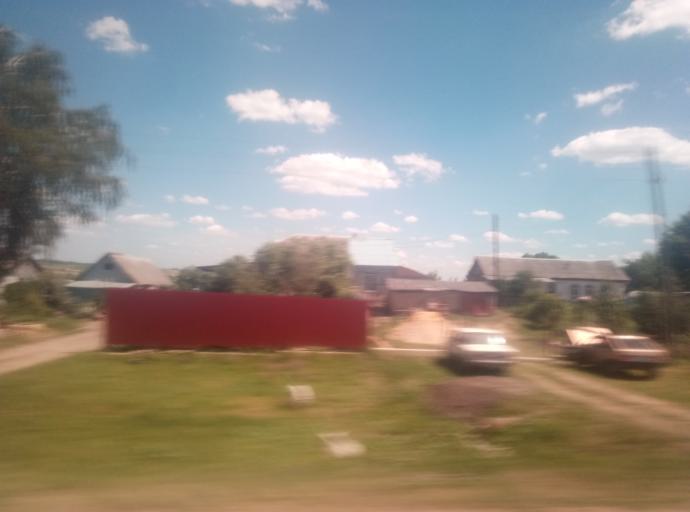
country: RU
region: Tula
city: Kireyevsk
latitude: 53.9654
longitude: 37.9359
